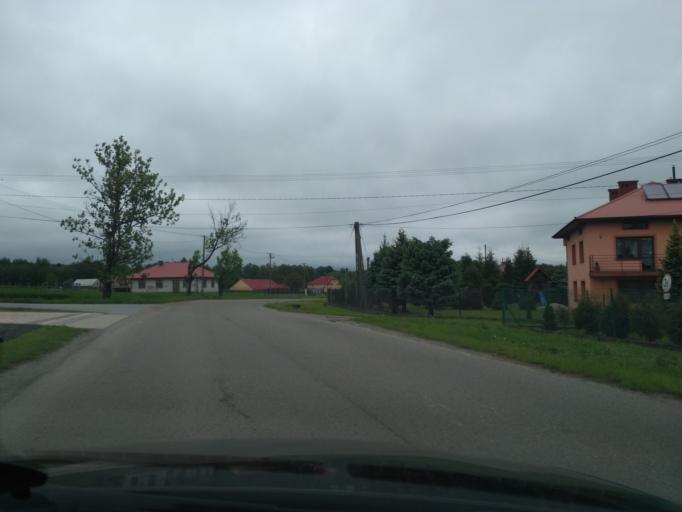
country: PL
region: Subcarpathian Voivodeship
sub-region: Powiat jasielski
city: Brzyska
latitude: 49.8405
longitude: 21.3877
